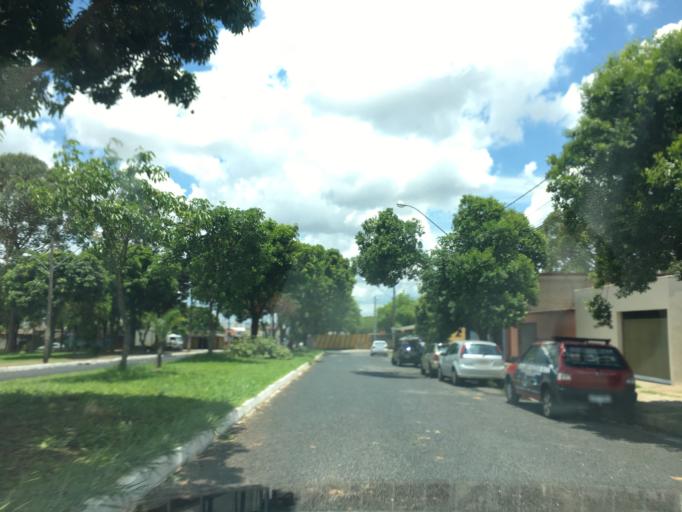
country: BR
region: Minas Gerais
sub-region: Uberlandia
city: Uberlandia
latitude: -18.9355
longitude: -48.3073
